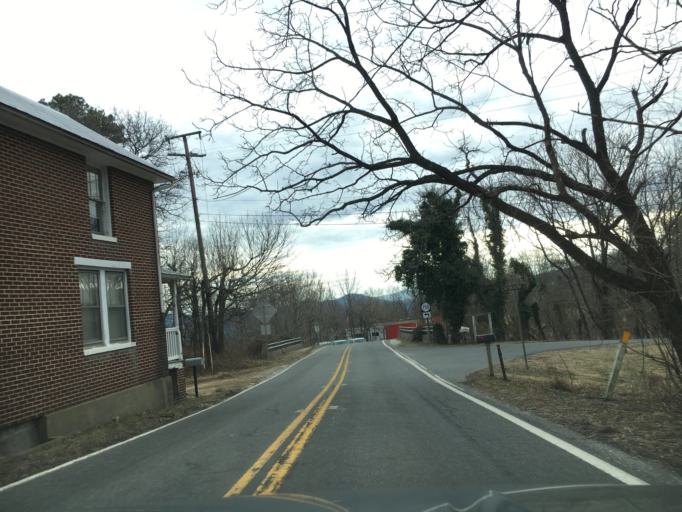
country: US
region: Virginia
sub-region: City of Waynesboro
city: Waynesboro
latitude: 38.0336
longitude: -78.8393
